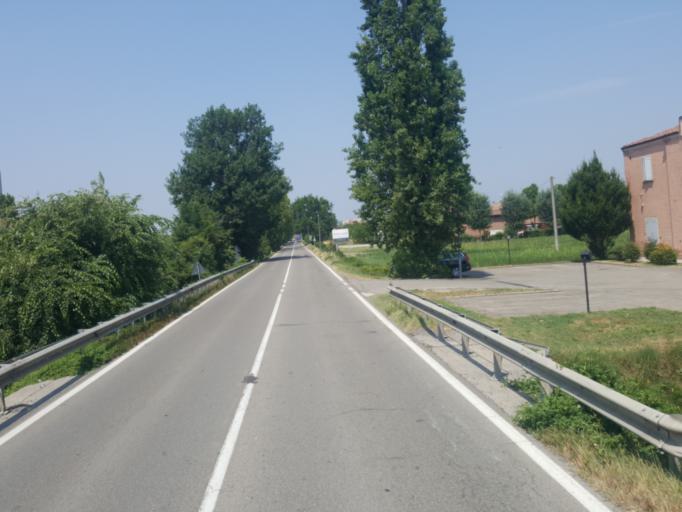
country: IT
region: Emilia-Romagna
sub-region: Provincia di Bologna
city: Calcara
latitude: 44.5555
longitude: 11.1661
